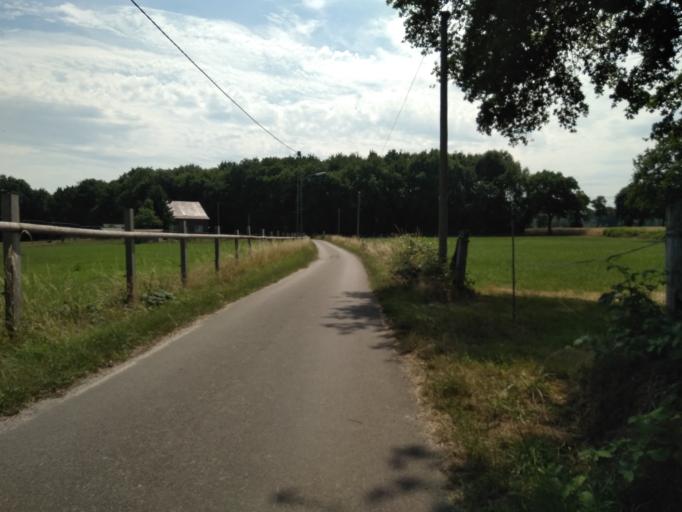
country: DE
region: North Rhine-Westphalia
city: Dorsten
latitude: 51.6495
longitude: 6.9392
